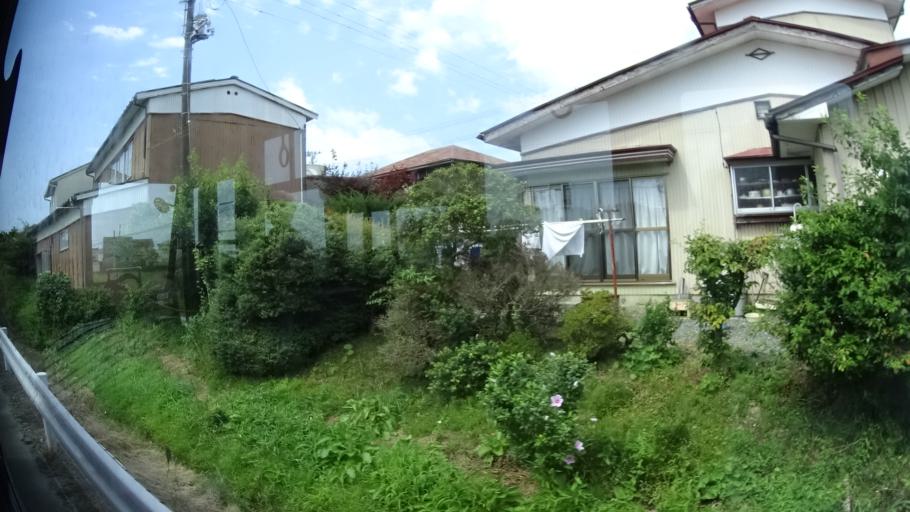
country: JP
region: Iwate
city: Ofunato
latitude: 38.8441
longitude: 141.5817
